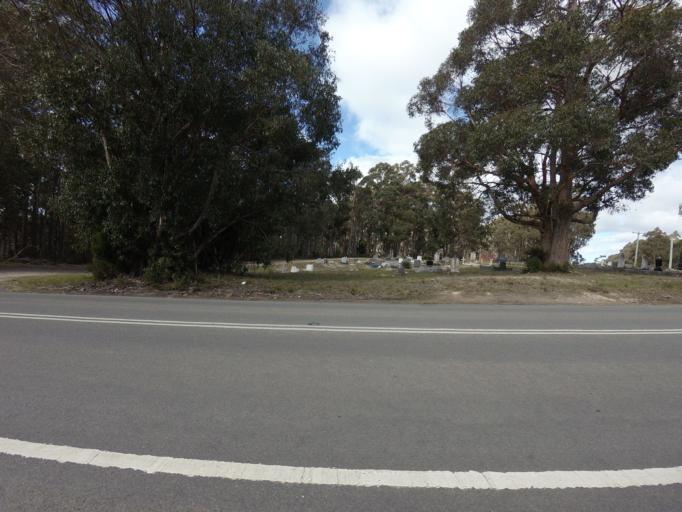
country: AU
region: Tasmania
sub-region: Huon Valley
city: Geeveston
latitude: -43.1969
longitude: 146.9568
